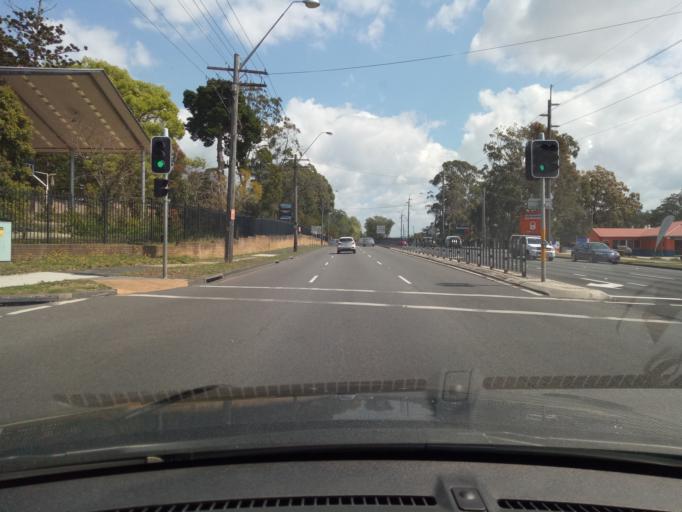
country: AU
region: New South Wales
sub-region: Gosford Shire
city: Erina
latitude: -33.4387
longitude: 151.3797
